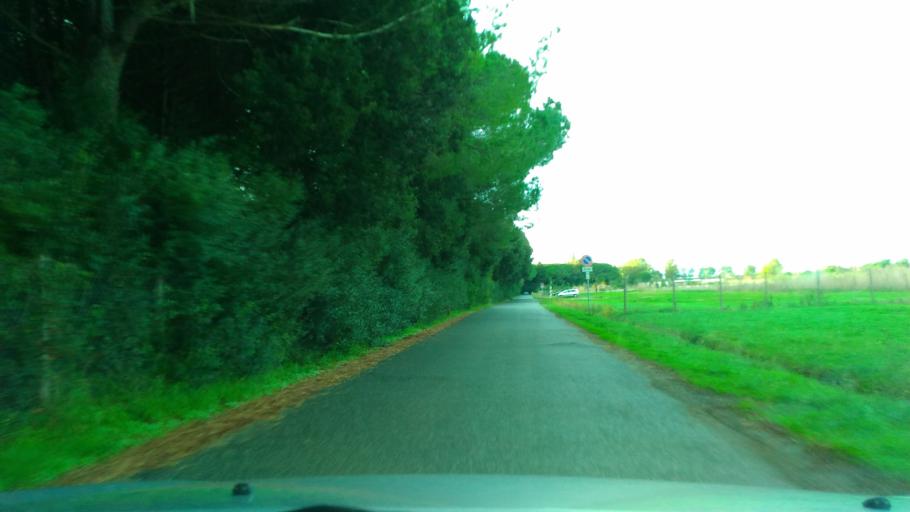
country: IT
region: Tuscany
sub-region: Provincia di Livorno
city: Cecina
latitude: 43.2890
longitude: 10.5083
